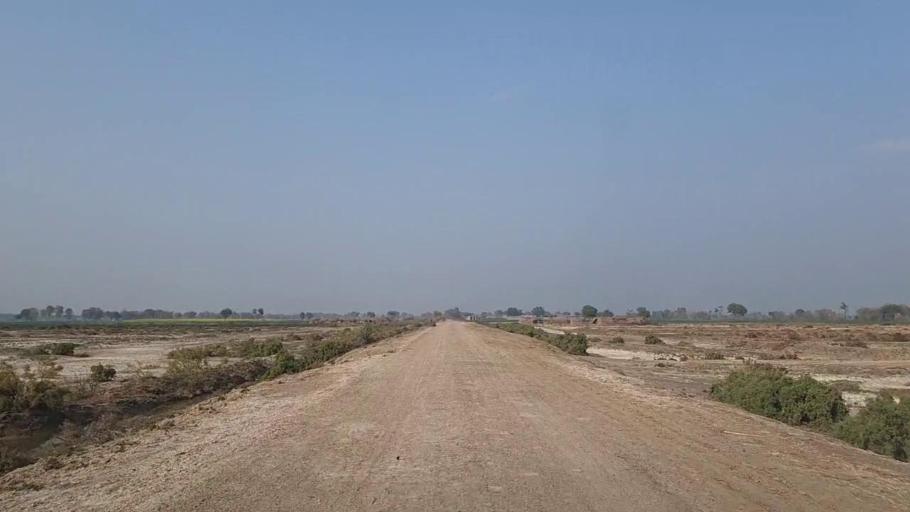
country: PK
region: Sindh
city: Nawabshah
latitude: 26.3451
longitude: 68.4740
